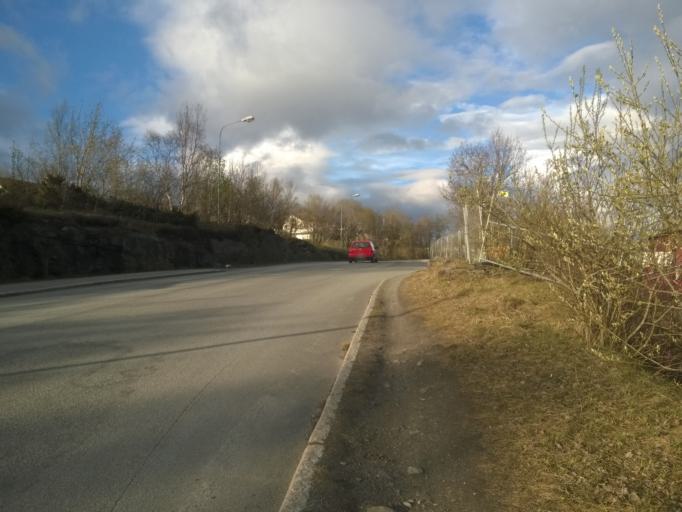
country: NO
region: Nordland
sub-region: Bodo
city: Lopsmarka
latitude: 67.2777
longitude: 14.5062
